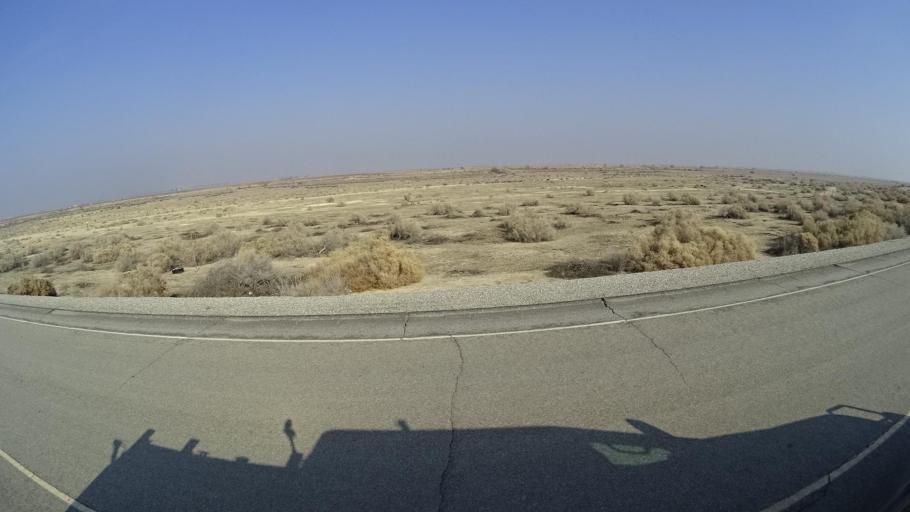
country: US
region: California
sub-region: Kern County
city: Buttonwillow
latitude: 35.3067
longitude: -119.3709
